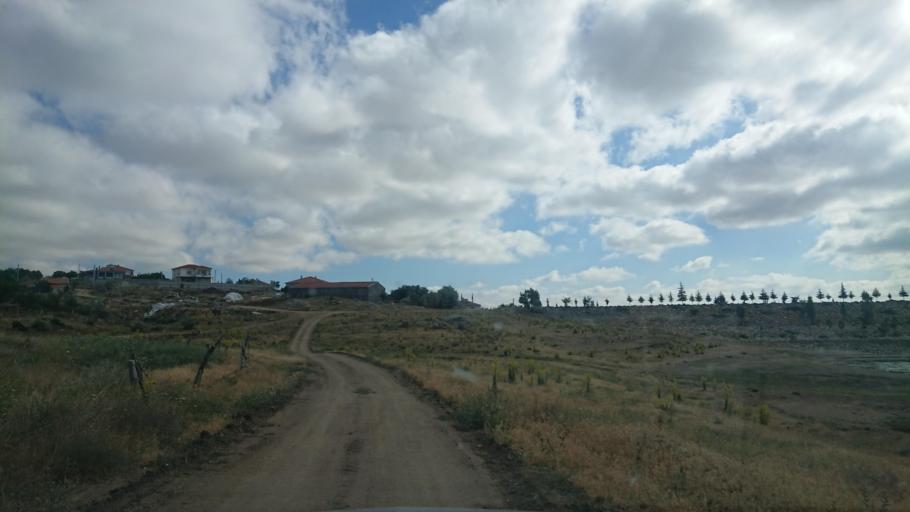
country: TR
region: Aksaray
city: Agacoren
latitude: 38.8653
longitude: 33.9469
